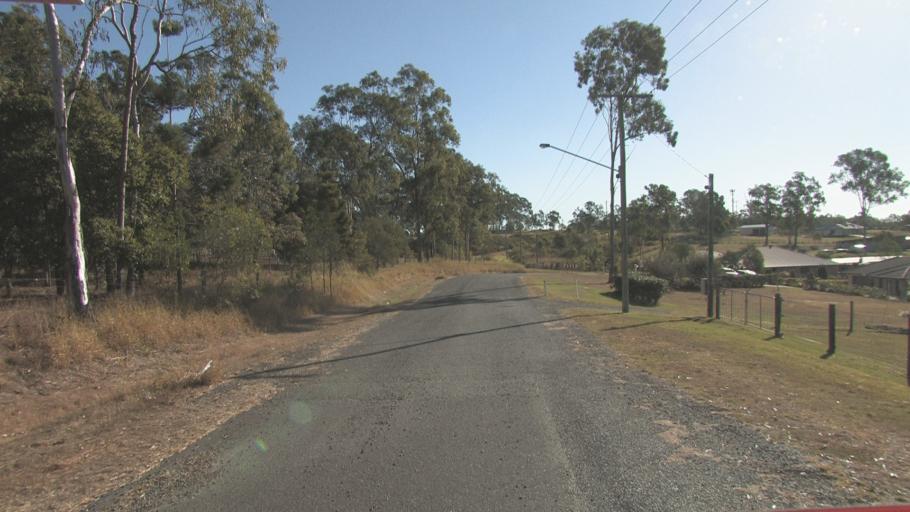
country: AU
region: Queensland
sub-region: Logan
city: North Maclean
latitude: -27.7955
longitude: 153.0210
